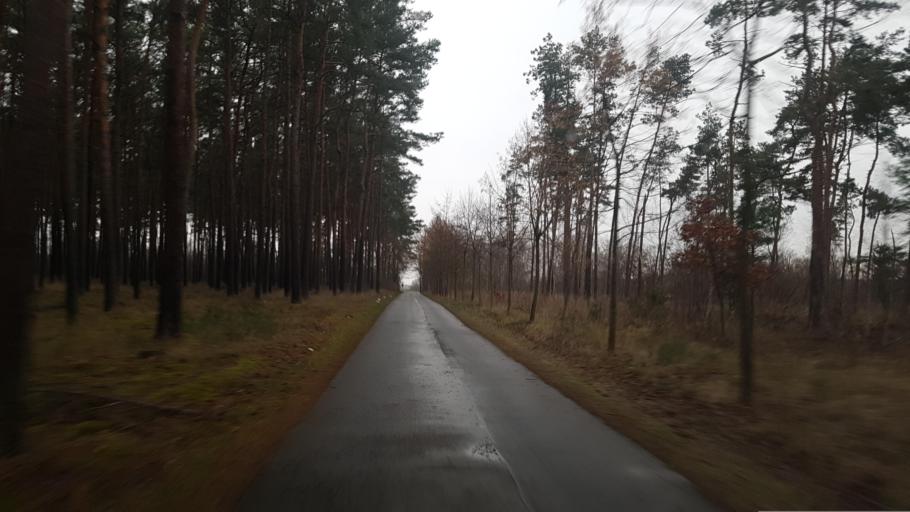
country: DE
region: Brandenburg
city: Cottbus
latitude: 51.6871
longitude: 14.3135
